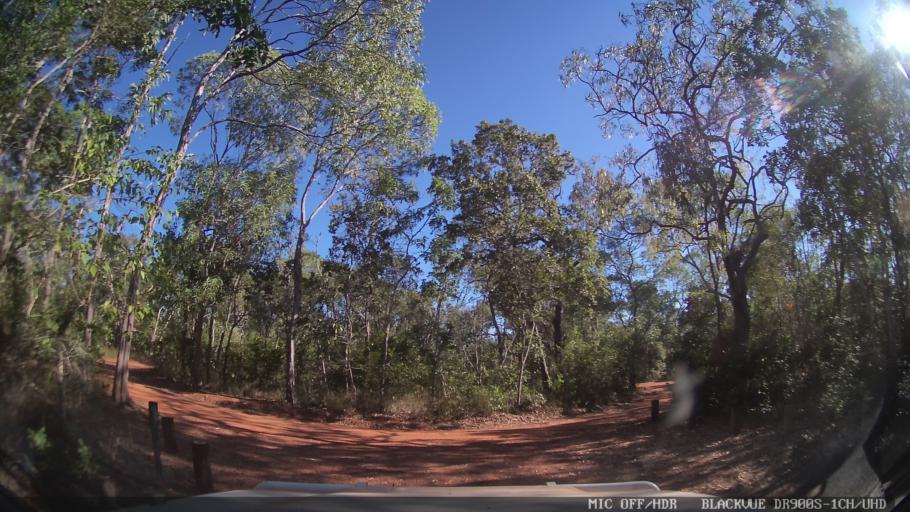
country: AU
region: Queensland
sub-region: Torres
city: Thursday Island
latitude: -11.3880
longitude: 142.4142
